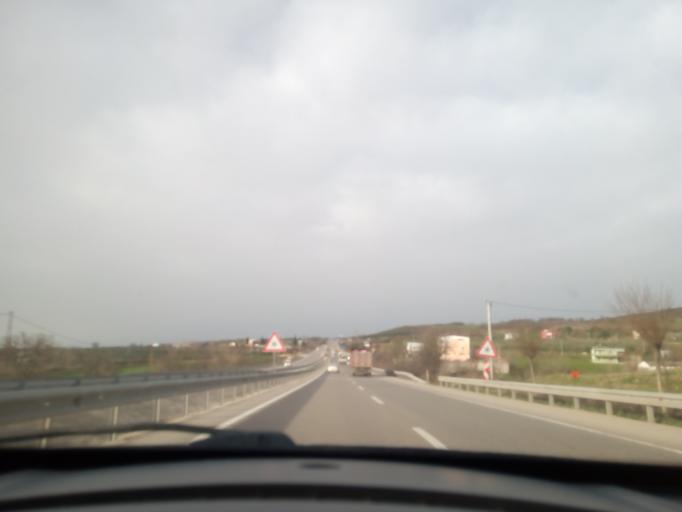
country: TR
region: Bursa
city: Gorukle
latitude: 40.2138
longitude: 28.7072
